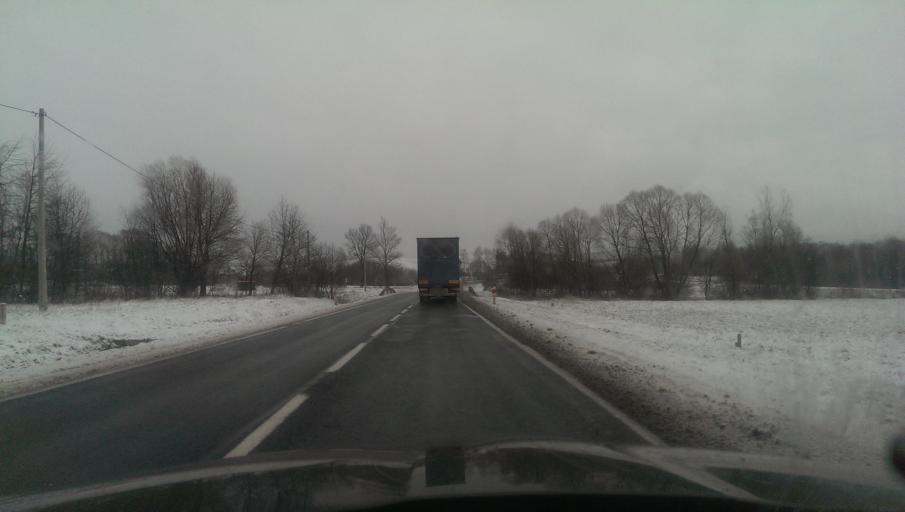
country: PL
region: Subcarpathian Voivodeship
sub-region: Powiat sanocki
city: Nowosielce-Gniewosz
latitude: 49.5630
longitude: 22.1174
